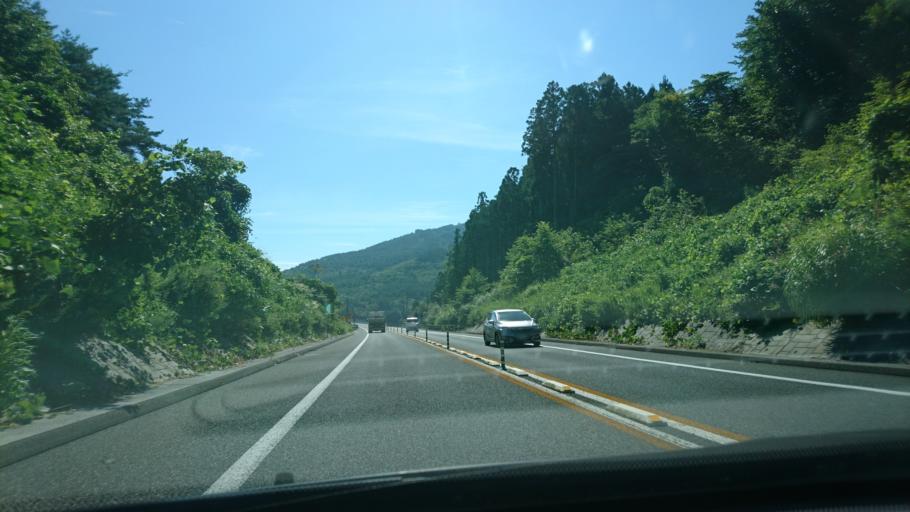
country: JP
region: Iwate
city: Kitakami
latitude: 39.2910
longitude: 141.3198
